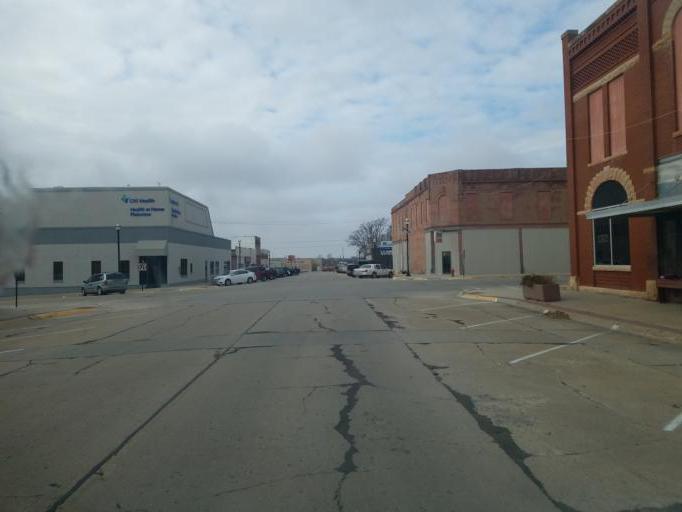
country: US
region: Nebraska
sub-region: Pierce County
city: Plainview
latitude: 42.3496
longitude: -97.7931
